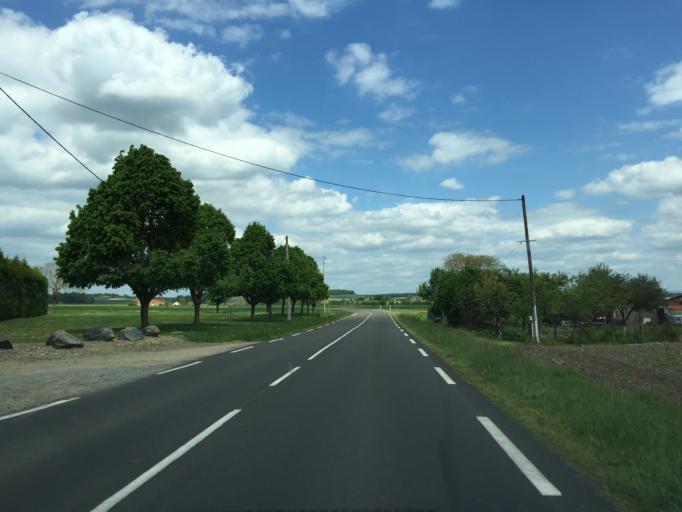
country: FR
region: Auvergne
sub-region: Departement du Puy-de-Dome
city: Aigueperse
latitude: 46.0463
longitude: 3.2613
